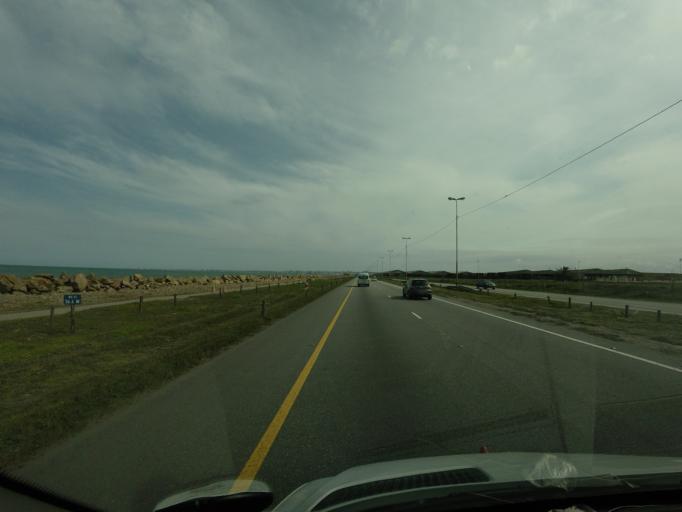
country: ZA
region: Eastern Cape
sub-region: Nelson Mandela Bay Metropolitan Municipality
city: Port Elizabeth
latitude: -33.8971
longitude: 25.6205
